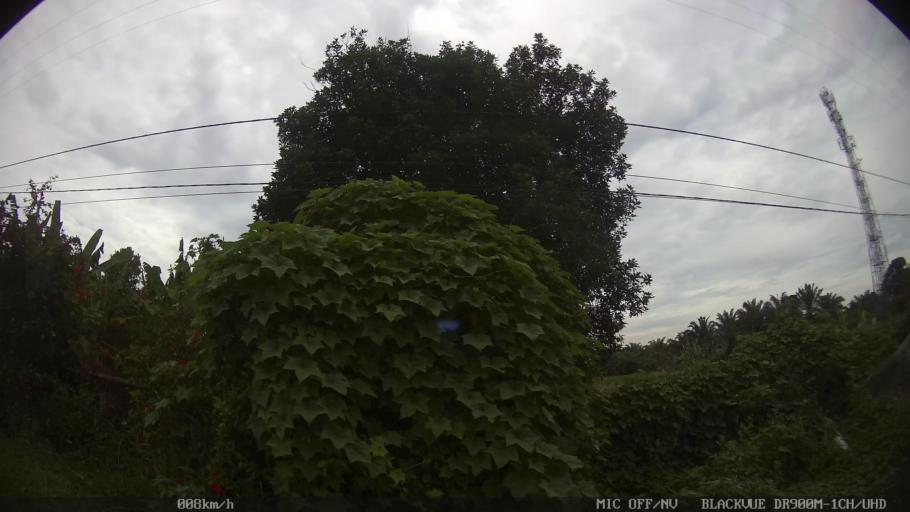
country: ID
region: North Sumatra
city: Sunggal
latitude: 3.5761
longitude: 98.5648
